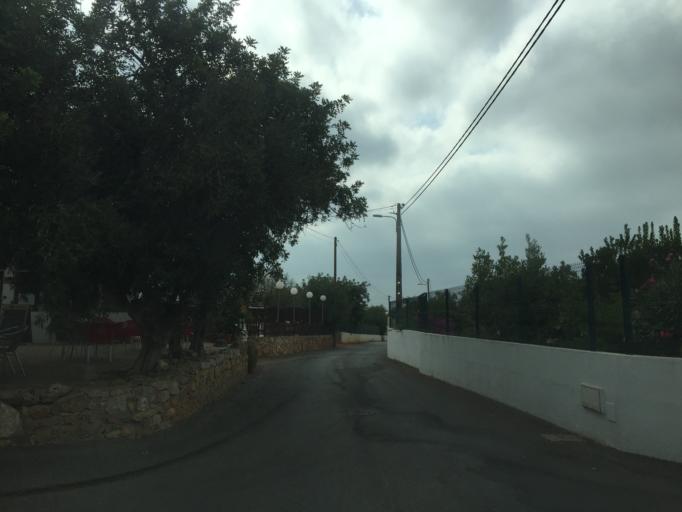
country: PT
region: Faro
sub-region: Loule
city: Almancil
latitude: 37.0972
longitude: -8.0262
